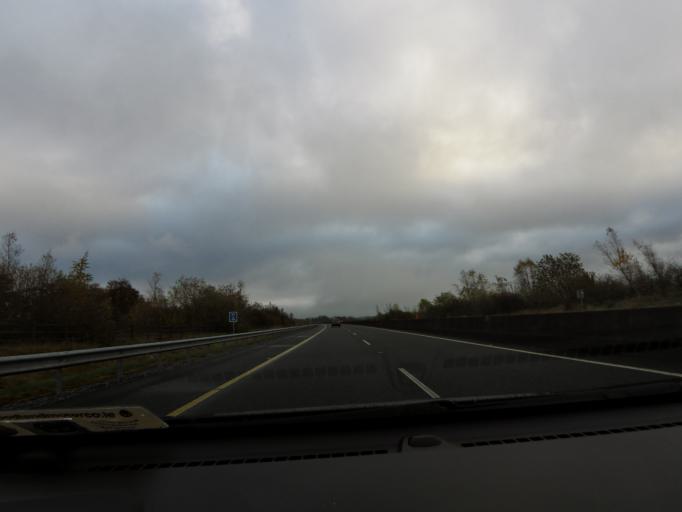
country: IE
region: Connaught
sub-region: County Galway
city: Ballinasloe
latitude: 53.2922
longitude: -8.3621
